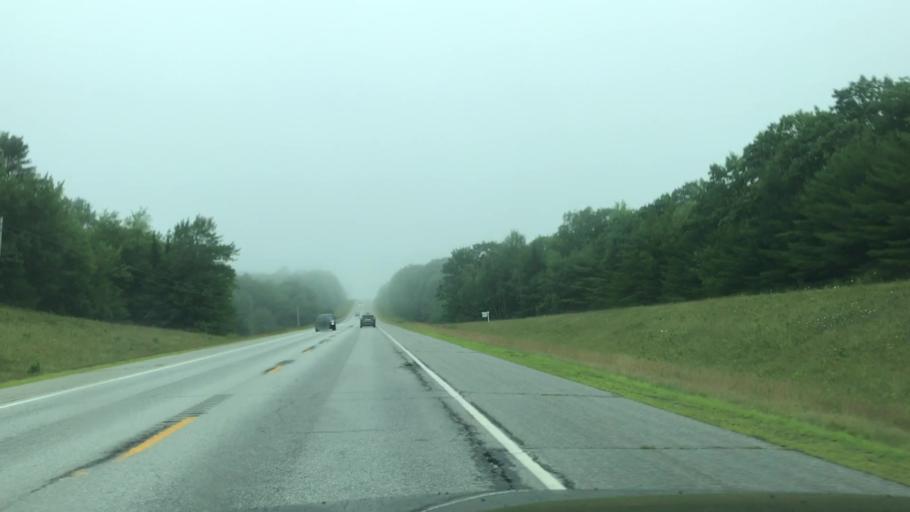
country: US
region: Maine
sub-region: Lincoln County
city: Nobleboro
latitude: 44.0660
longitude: -69.4890
